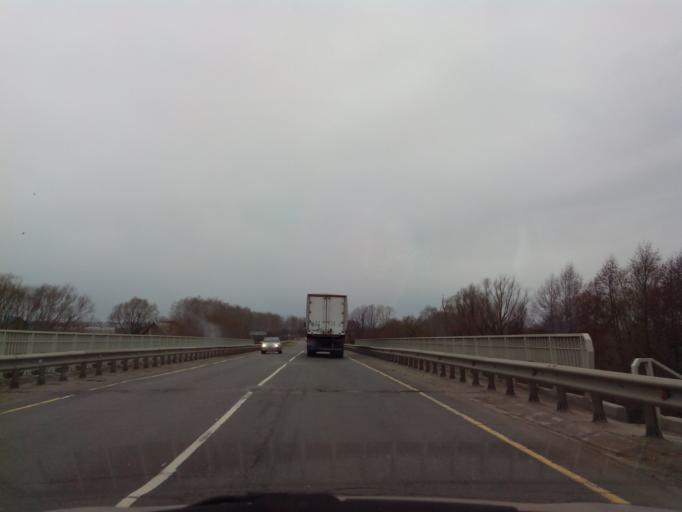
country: RU
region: Tambov
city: Pokrovo-Prigorodnoye
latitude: 52.6771
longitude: 41.3259
